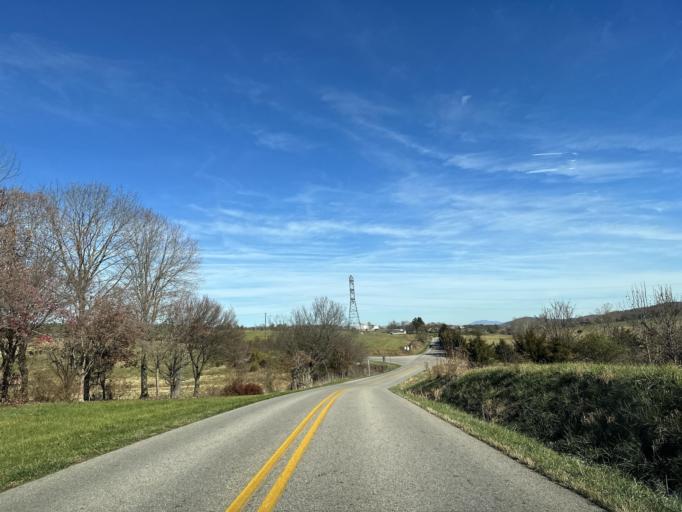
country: US
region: Virginia
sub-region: Augusta County
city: Fishersville
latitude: 38.1271
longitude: -78.9472
